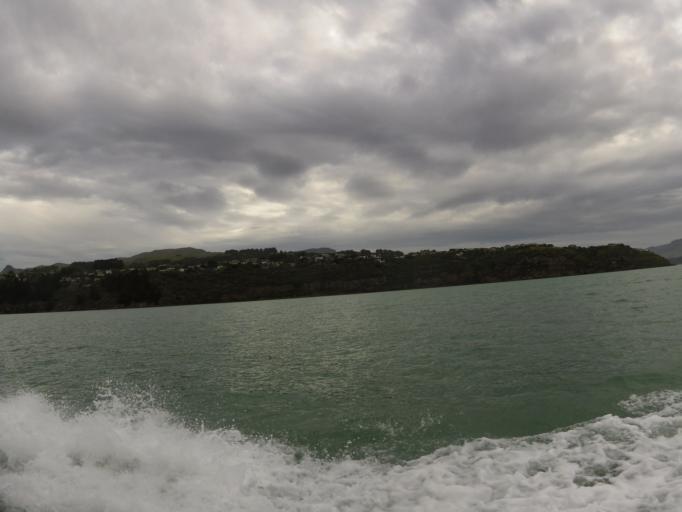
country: NZ
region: Canterbury
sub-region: Christchurch City
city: Christchurch
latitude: -43.6193
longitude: 172.7290
